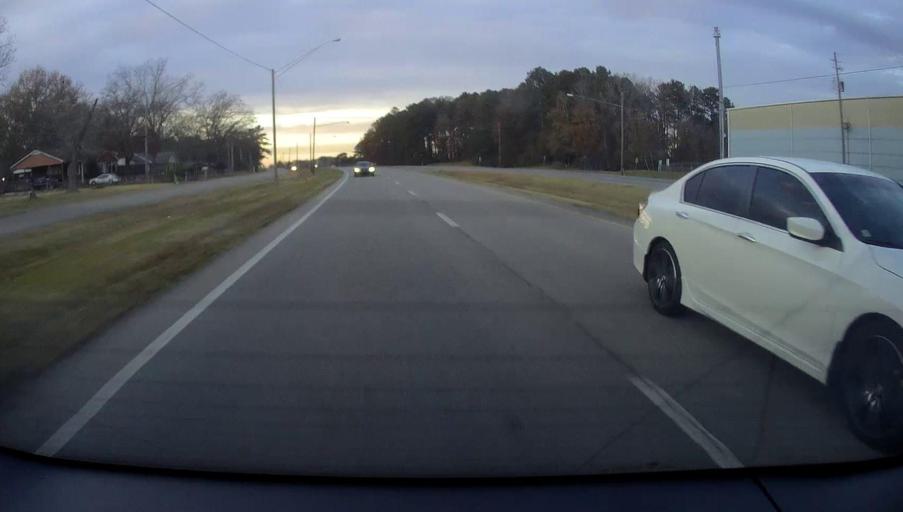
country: US
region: Alabama
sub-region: Etowah County
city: Glencoe
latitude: 33.9803
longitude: -85.9574
